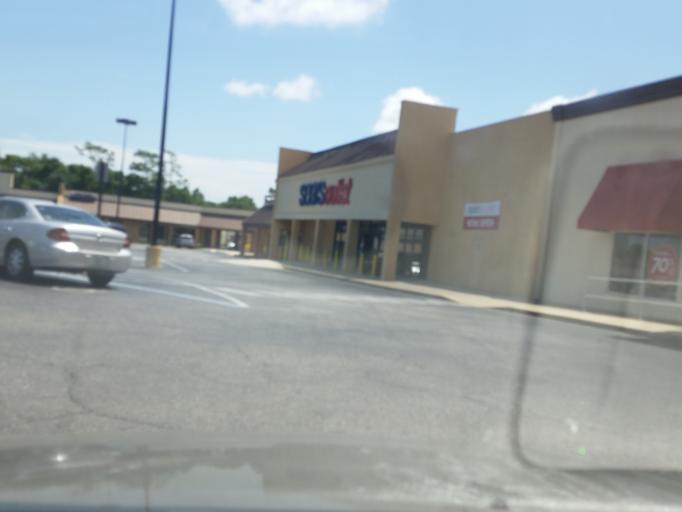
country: US
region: Florida
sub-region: Escambia County
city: Brent
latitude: 30.4883
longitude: -87.2250
